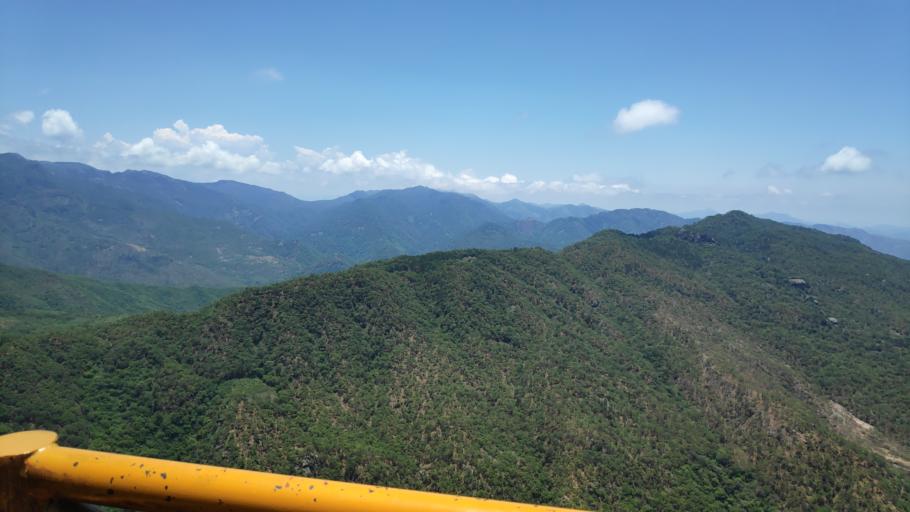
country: MX
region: Sinaloa
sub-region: Sinaloa
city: Bacubirito
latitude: 25.7452
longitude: -107.5503
